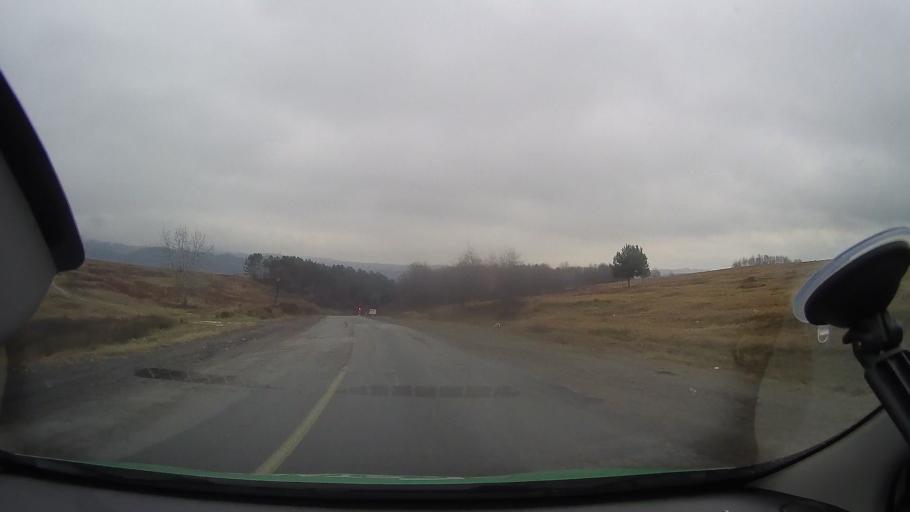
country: RO
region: Arad
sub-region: Comuna Halmagiu
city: Halmagiu
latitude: 46.2812
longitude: 22.5855
